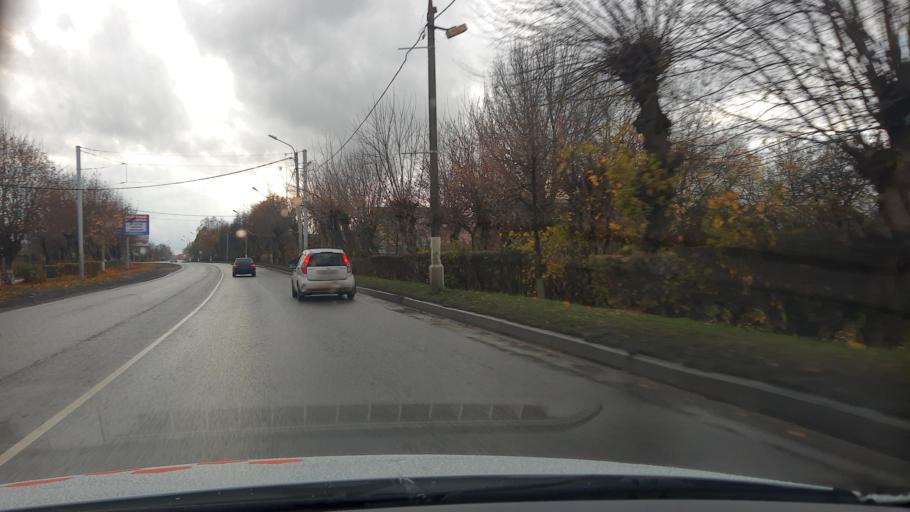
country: RU
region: Moskovskaya
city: Noginsk
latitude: 55.8376
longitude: 38.3909
